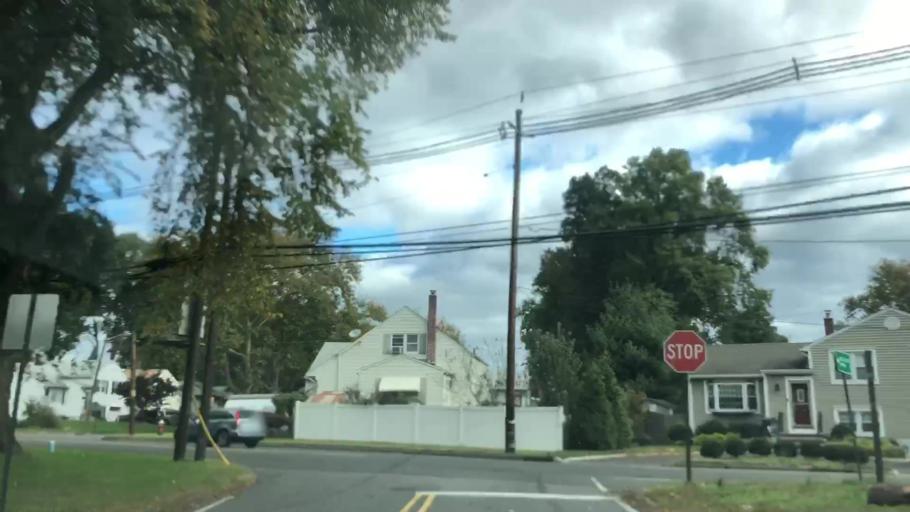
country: US
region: New Jersey
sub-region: Union County
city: Winfield
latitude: 40.6358
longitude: -74.2840
